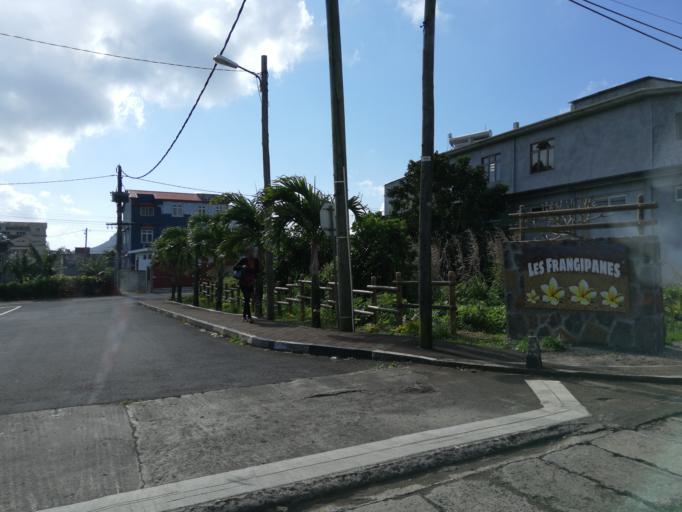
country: MU
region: Moka
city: Verdun
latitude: -20.2210
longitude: 57.5483
